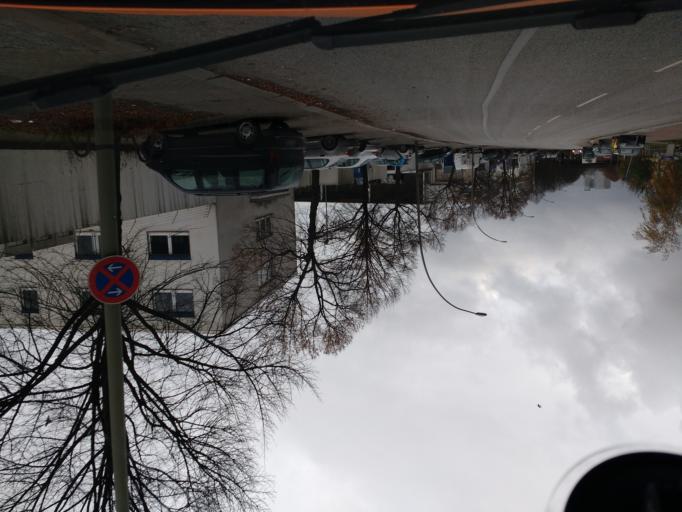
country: DE
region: Hamburg
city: Rothenburgsort
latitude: 53.5409
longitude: 10.0410
